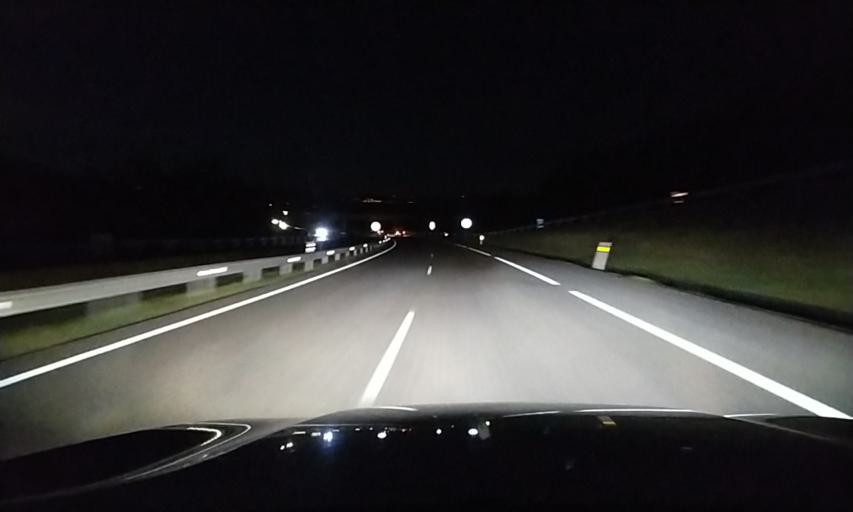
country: ES
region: Galicia
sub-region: Provincia de Ourense
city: Ambia
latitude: 42.1524
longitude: -7.7554
